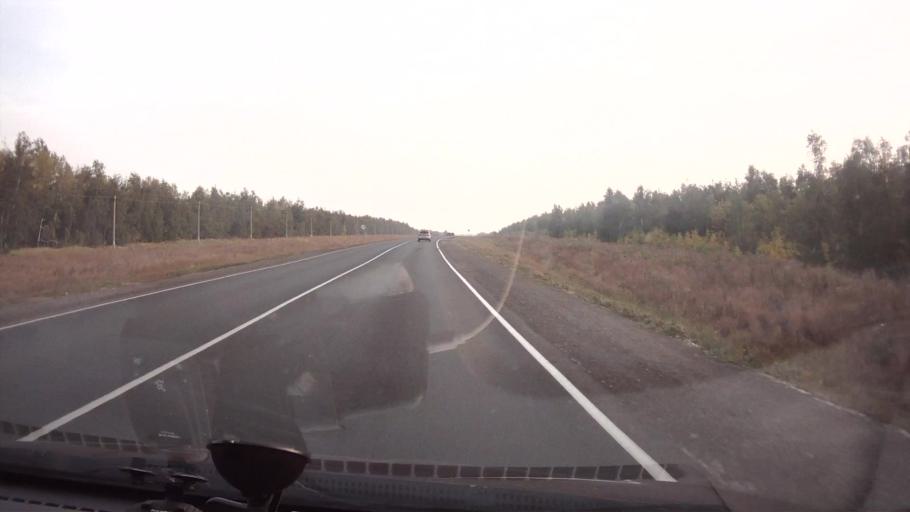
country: RU
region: Saratov
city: Krasnyy Oktyabr'
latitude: 51.3768
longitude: 45.7123
